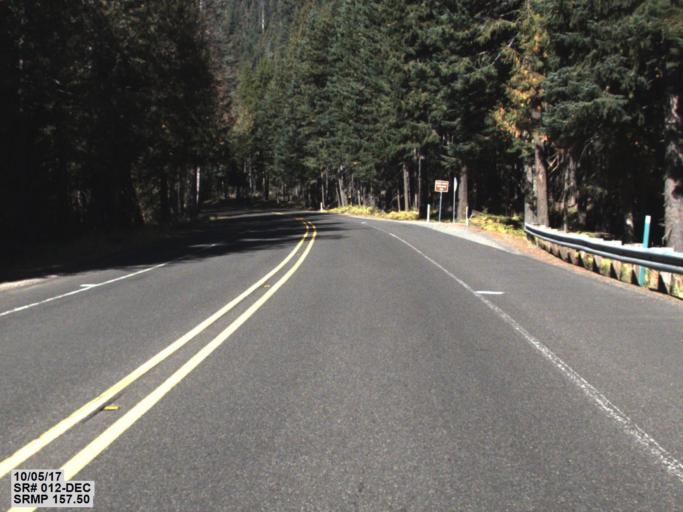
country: US
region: Washington
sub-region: Yakima County
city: Tieton
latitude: 46.6495
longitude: -121.2782
